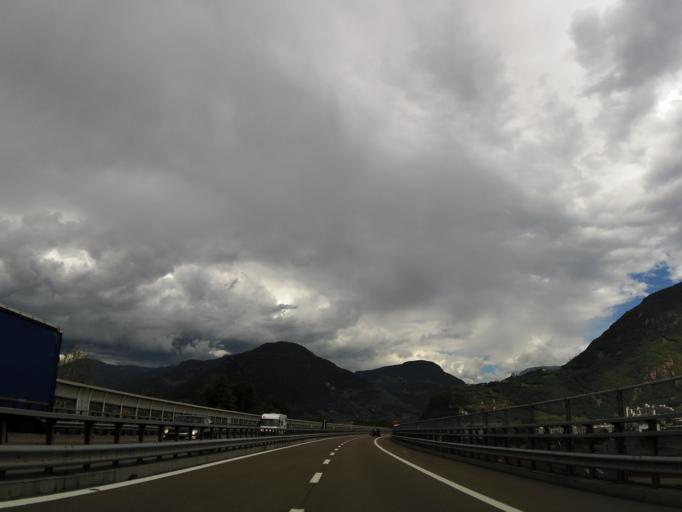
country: IT
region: Trentino-Alto Adige
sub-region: Bolzano
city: Bolzano
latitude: 46.4848
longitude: 11.3286
